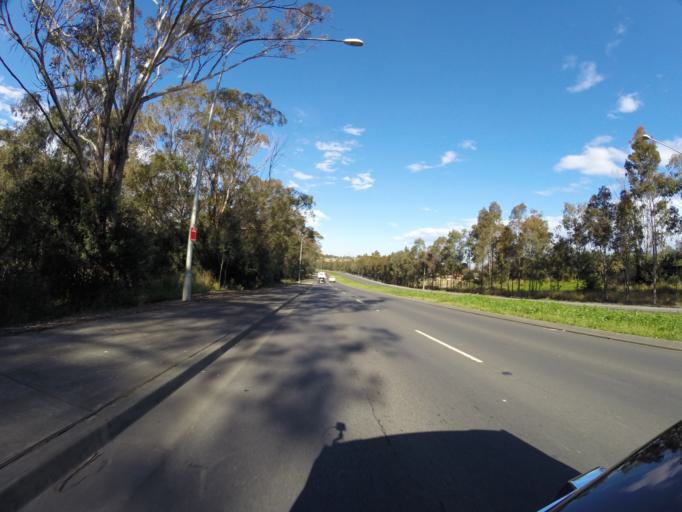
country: AU
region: New South Wales
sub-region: Fairfield
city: Cecil Park
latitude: -33.8810
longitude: 150.8492
